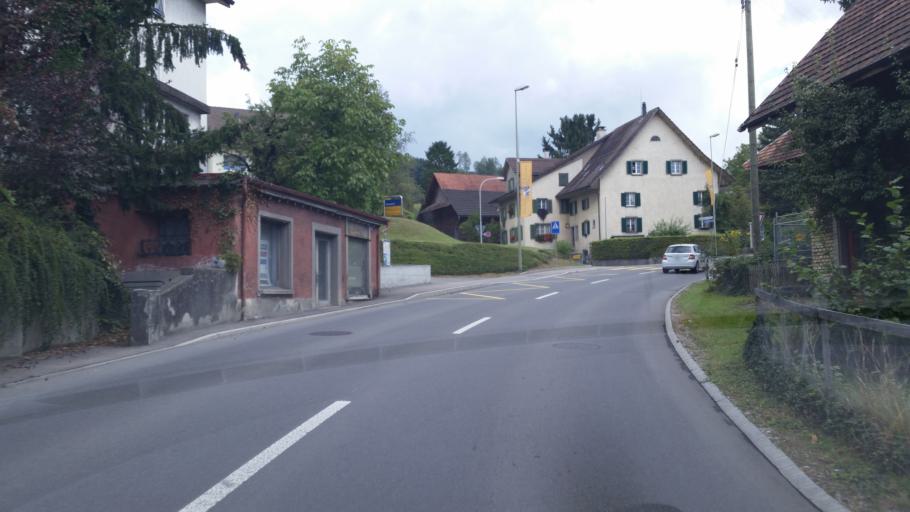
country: CH
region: Zurich
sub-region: Bezirk Affoltern
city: Mettmenstetten
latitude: 47.2464
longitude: 8.4679
